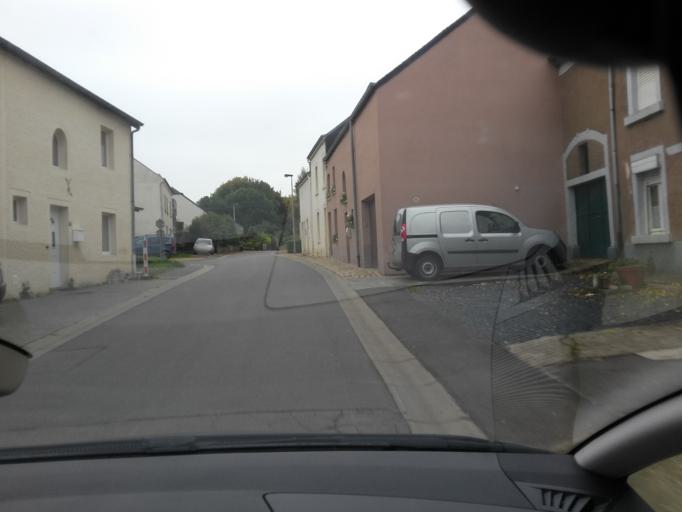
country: BE
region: Wallonia
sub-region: Province du Luxembourg
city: Arlon
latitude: 49.7089
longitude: 5.8202
